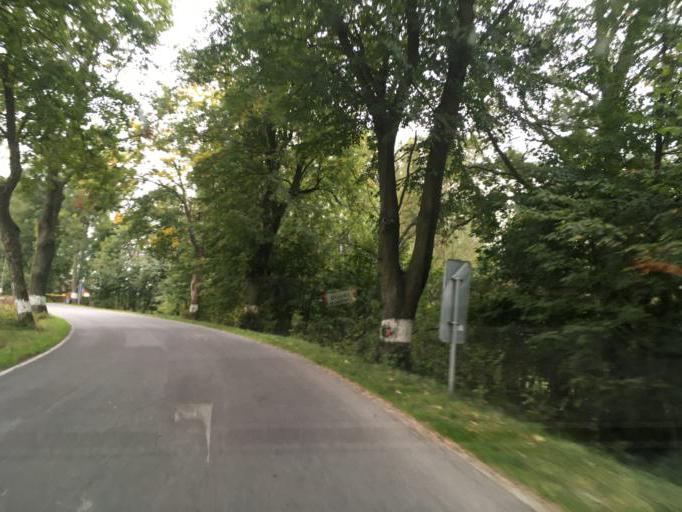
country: CZ
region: Vysocina
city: Horni Cerekev
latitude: 49.3174
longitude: 15.3310
